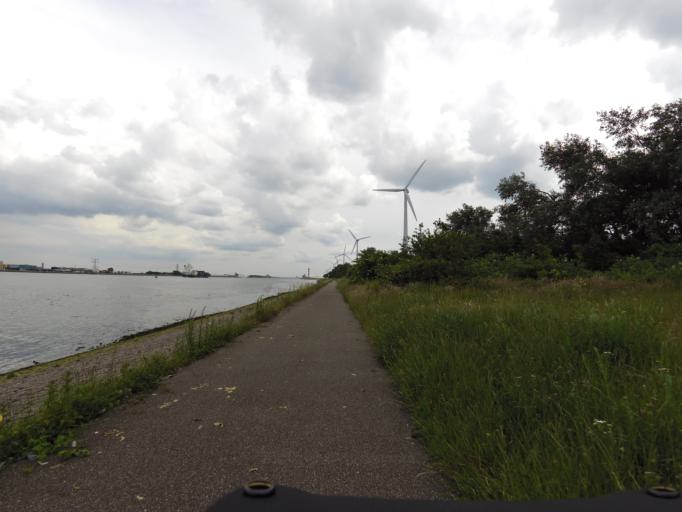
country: NL
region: South Holland
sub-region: Gemeente Rotterdam
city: Hoek van Holland
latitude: 51.9651
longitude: 4.1356
